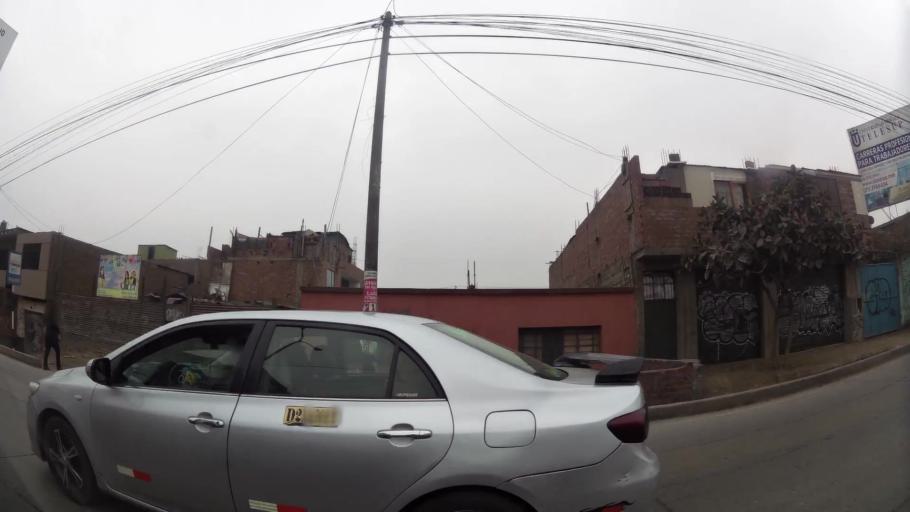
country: PE
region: Lima
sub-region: Lima
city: Vitarte
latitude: -12.0237
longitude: -76.9130
